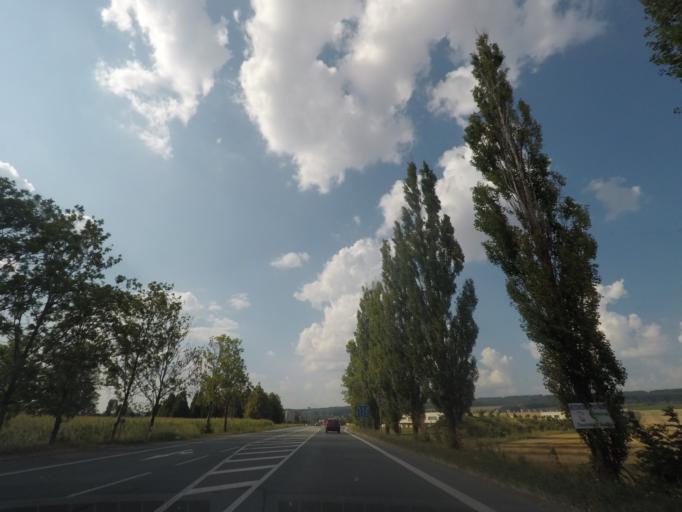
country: CZ
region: Kralovehradecky
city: Dvur Kralove nad Labem
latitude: 50.4186
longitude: 15.8830
